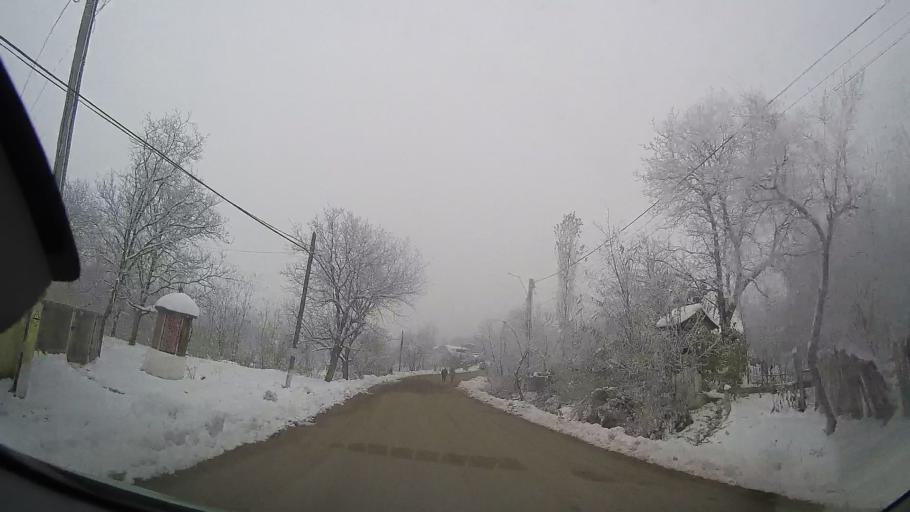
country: RO
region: Iasi
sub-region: Comuna Tansa
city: Tansa
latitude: 46.9061
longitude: 27.2423
